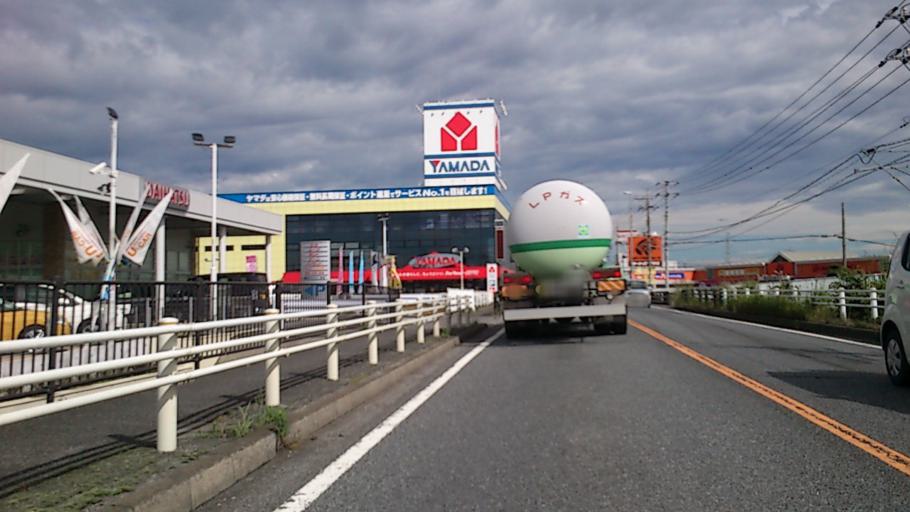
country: JP
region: Saitama
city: Honjo
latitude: 36.2407
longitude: 139.2024
